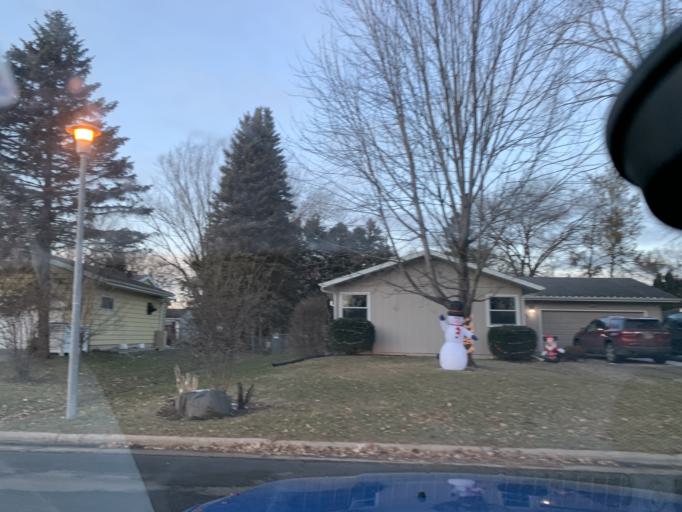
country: US
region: Wisconsin
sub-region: Dane County
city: Shorewood Hills
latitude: 43.0259
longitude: -89.4720
